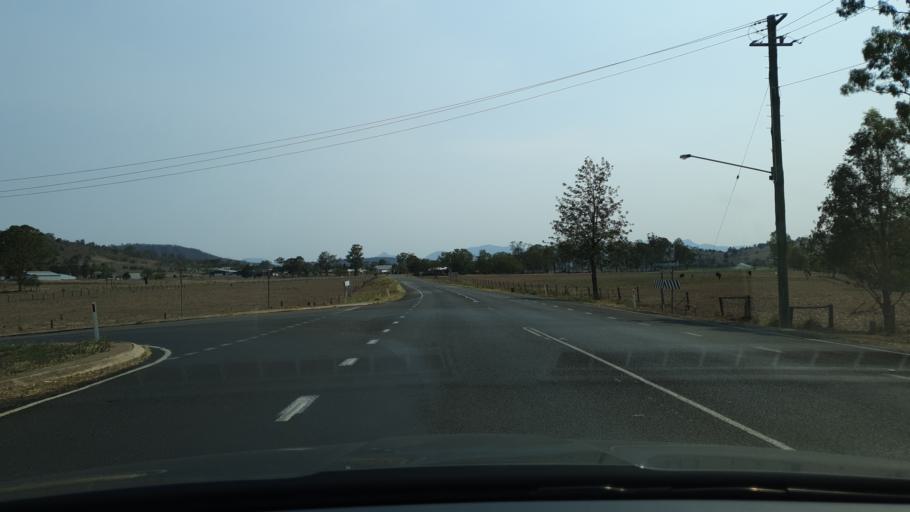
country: AU
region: Queensland
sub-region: Ipswich
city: Deebing Heights
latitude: -28.0083
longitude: 152.6797
